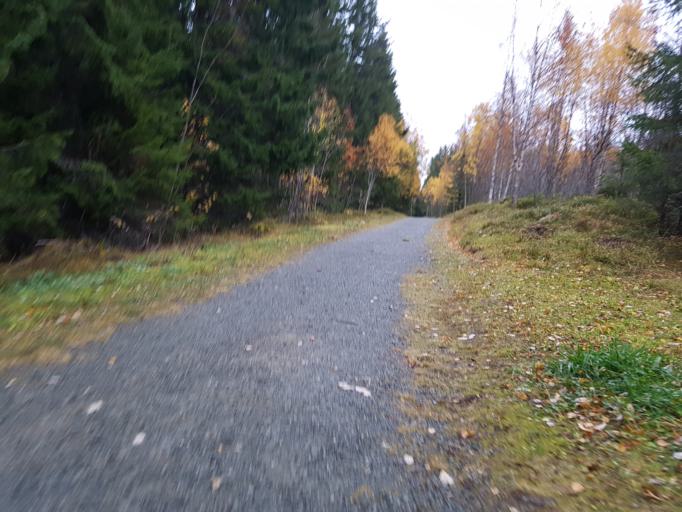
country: NO
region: Sor-Trondelag
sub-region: Trondheim
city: Trondheim
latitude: 63.3809
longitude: 10.3253
